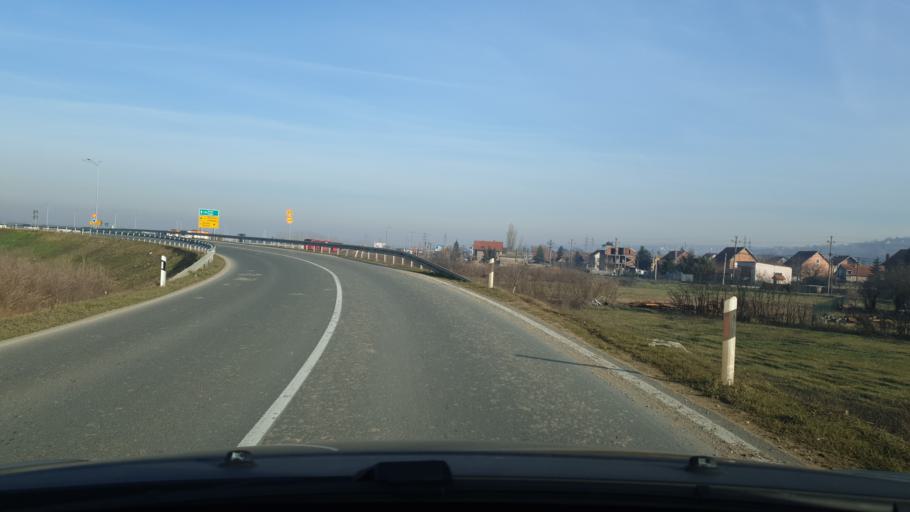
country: RS
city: Baric
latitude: 44.6487
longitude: 20.2312
